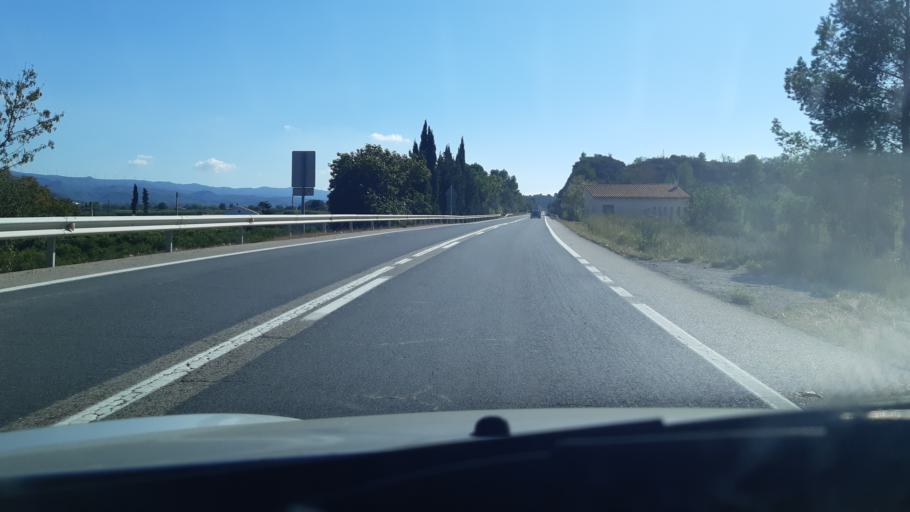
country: ES
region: Catalonia
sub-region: Provincia de Tarragona
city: Tivenys
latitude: 40.8956
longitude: 0.4885
